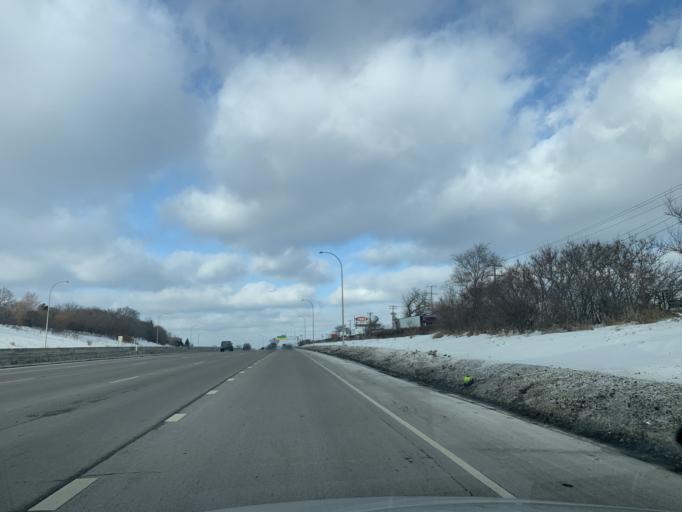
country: US
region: Minnesota
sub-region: Anoka County
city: Columbia Heights
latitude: 45.0159
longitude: -93.2823
